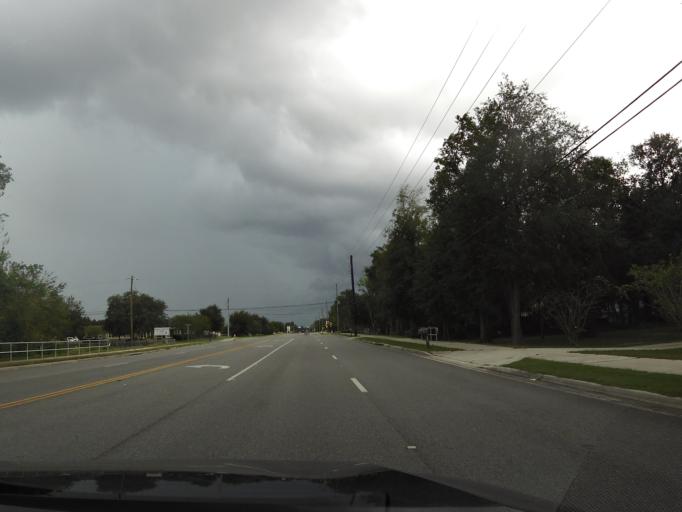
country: US
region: Florida
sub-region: Clay County
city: Asbury Lake
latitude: 30.0527
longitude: -81.8095
